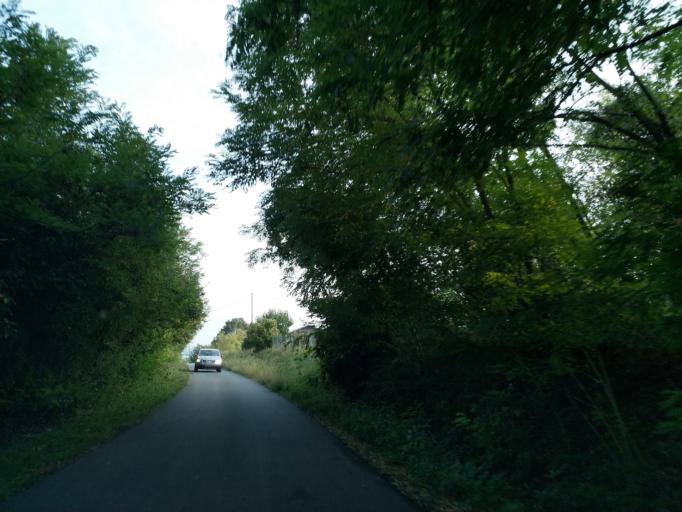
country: RS
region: Central Serbia
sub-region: Sumadijski Okrug
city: Arangelovac
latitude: 44.3108
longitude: 20.5907
